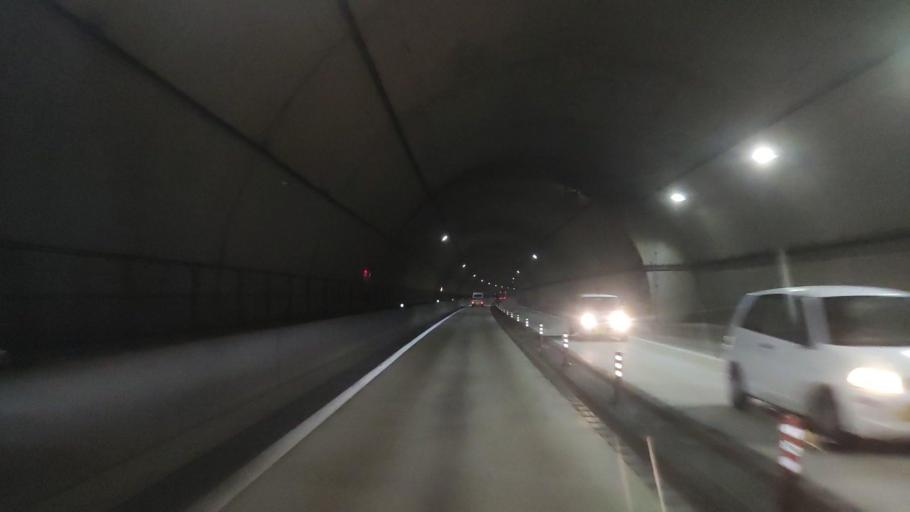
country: JP
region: Wakayama
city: Tanabe
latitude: 33.5895
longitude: 135.4415
